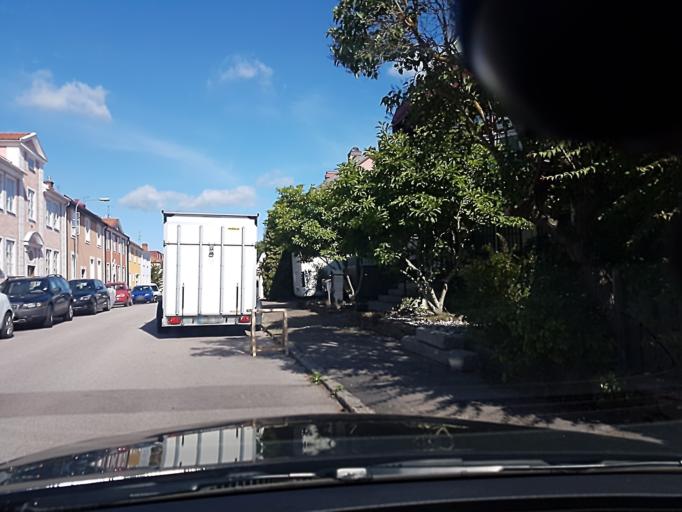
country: SE
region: Kalmar
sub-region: Kalmar Kommun
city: Kalmar
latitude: 56.6588
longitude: 16.3459
